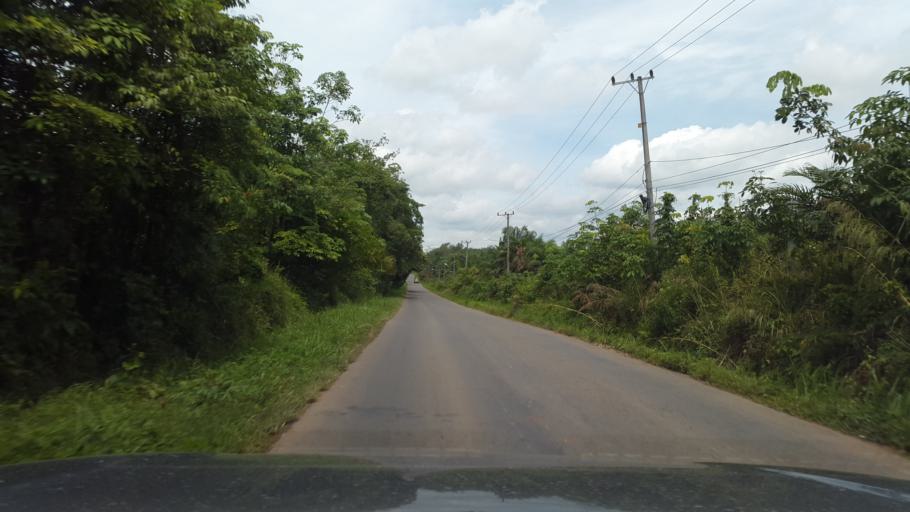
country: ID
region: South Sumatra
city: Gunungmegang Dalam
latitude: -3.3791
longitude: 103.9491
